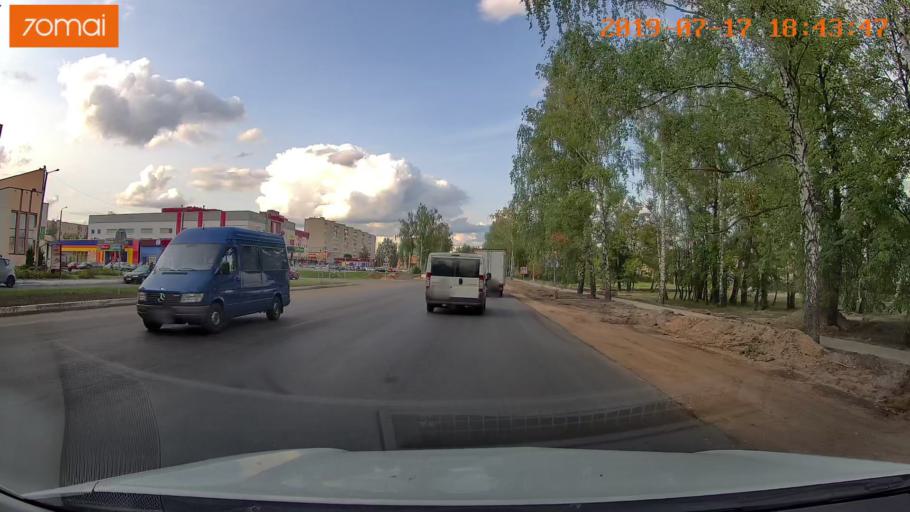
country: BY
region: Mogilev
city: Asipovichy
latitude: 53.3169
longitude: 28.6449
